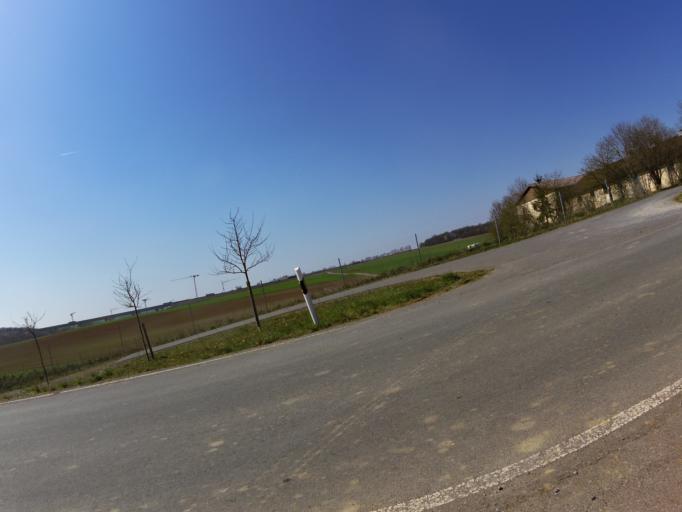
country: DE
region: Bavaria
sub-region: Regierungsbezirk Unterfranken
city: Rottendorf
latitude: 49.8102
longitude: 10.0562
